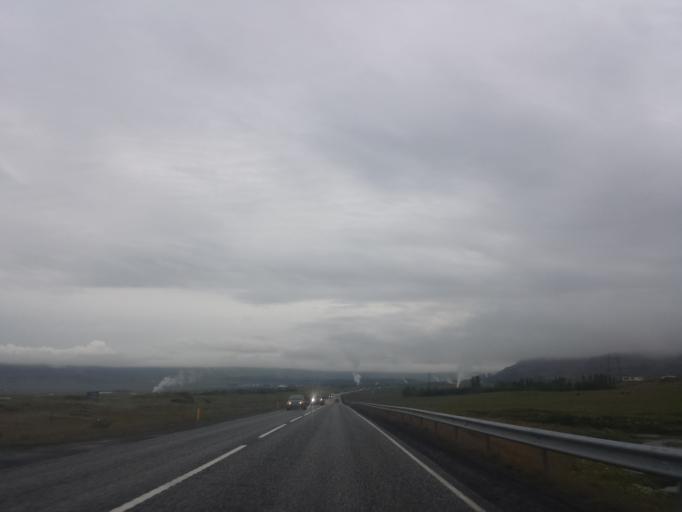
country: IS
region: South
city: Hveragerdi
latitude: 63.9730
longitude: -21.1403
